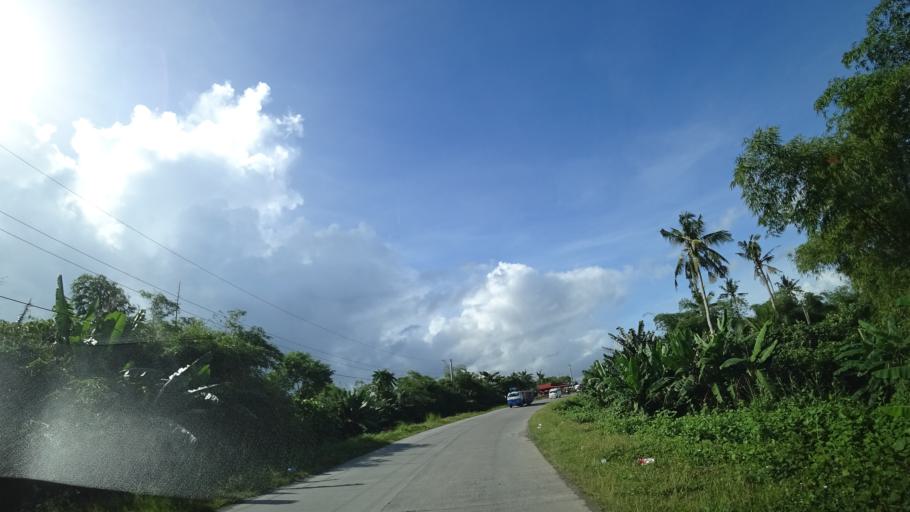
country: PH
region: Eastern Visayas
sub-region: Province of Leyte
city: Palo
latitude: 11.1612
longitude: 125.0031
